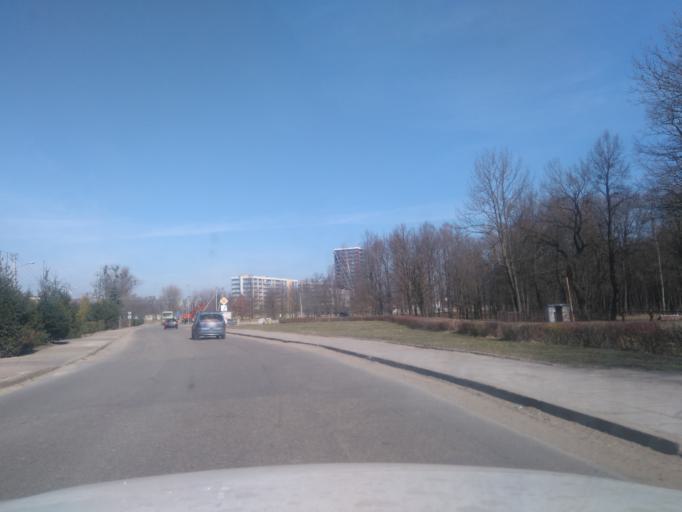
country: LT
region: Kauno apskritis
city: Dainava (Kaunas)
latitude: 54.8803
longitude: 23.9488
